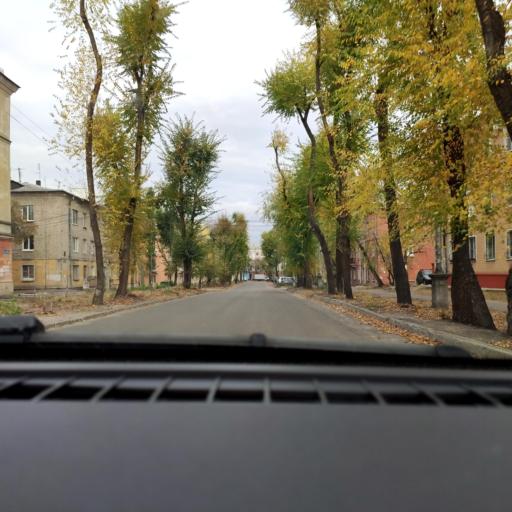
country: RU
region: Voronezj
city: Voronezh
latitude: 51.6320
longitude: 39.2361
